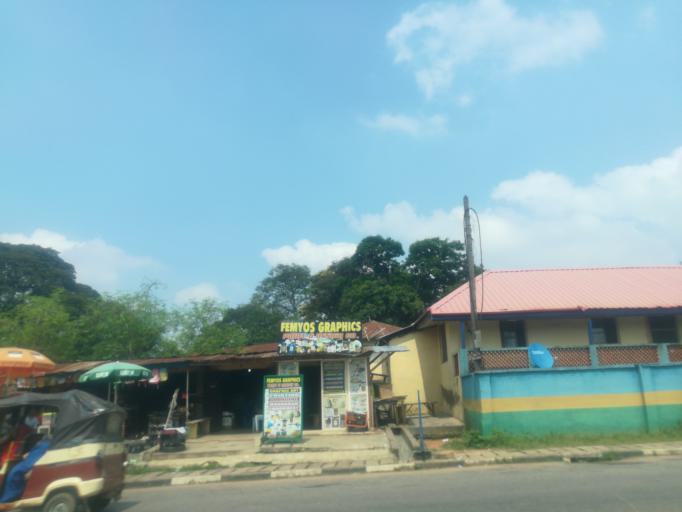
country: NG
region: Oyo
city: Ibadan
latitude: 7.3958
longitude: 3.9072
